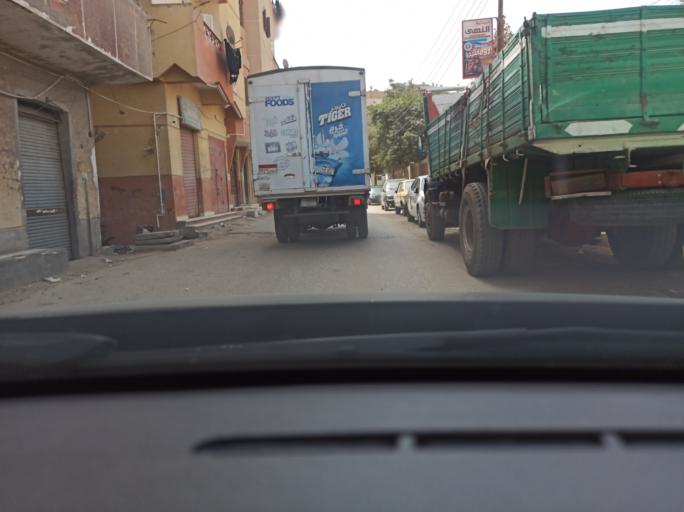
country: EG
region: Muhafazat Bani Suwayf
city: Bani Suwayf
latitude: 29.0782
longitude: 31.0876
